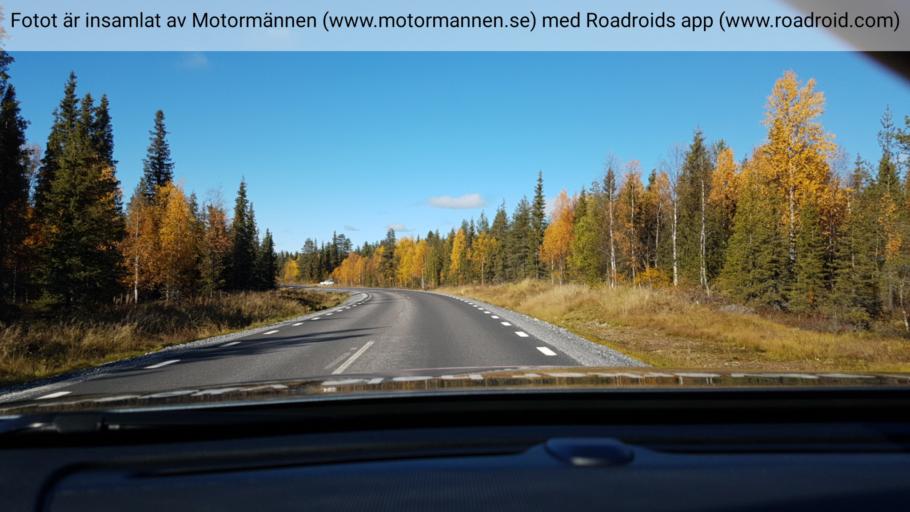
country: SE
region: Norrbotten
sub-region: Gallivare Kommun
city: Gaellivare
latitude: 66.8749
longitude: 20.9638
